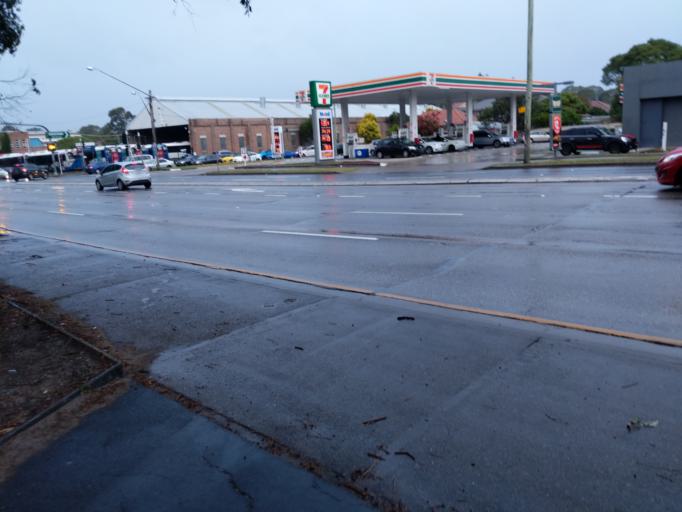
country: AU
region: New South Wales
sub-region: Ashfield
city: Croydon
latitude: -33.8691
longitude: 151.1080
